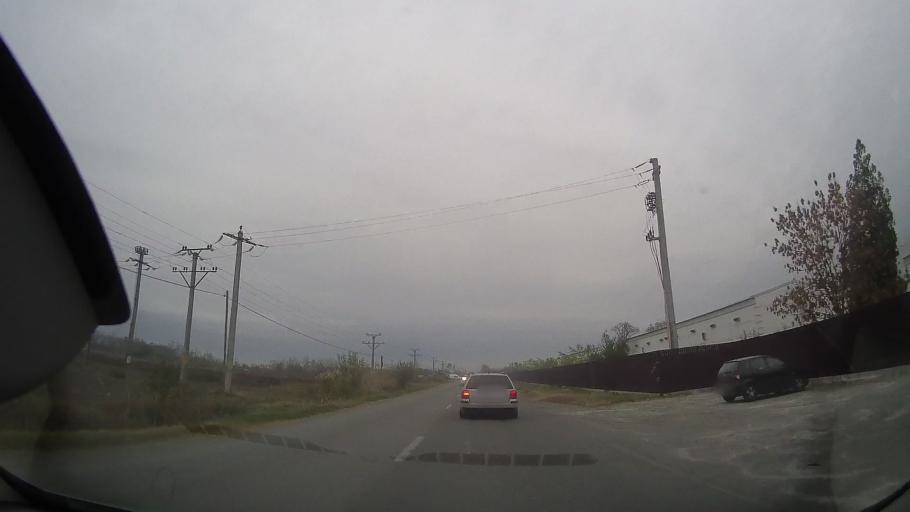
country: RO
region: Ialomita
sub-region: Oras Amara
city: Amara
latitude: 44.5890
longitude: 27.3311
